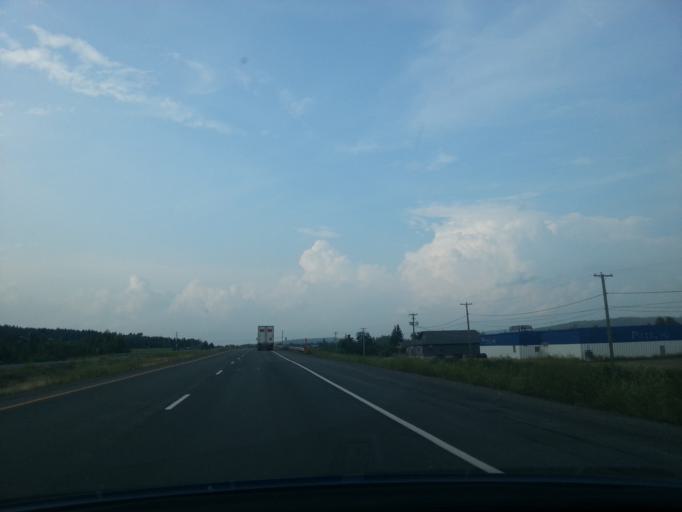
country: US
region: Maine
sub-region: Aroostook County
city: Fort Fairfield
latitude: 46.7456
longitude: -67.7145
